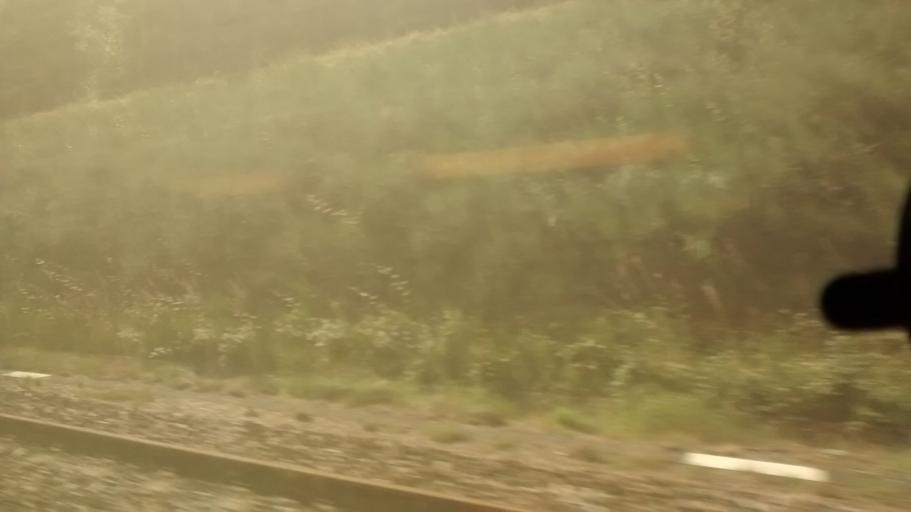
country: FR
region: Pays de la Loire
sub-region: Departement de la Sarthe
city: Le Luart
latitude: 48.0725
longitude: 0.6549
